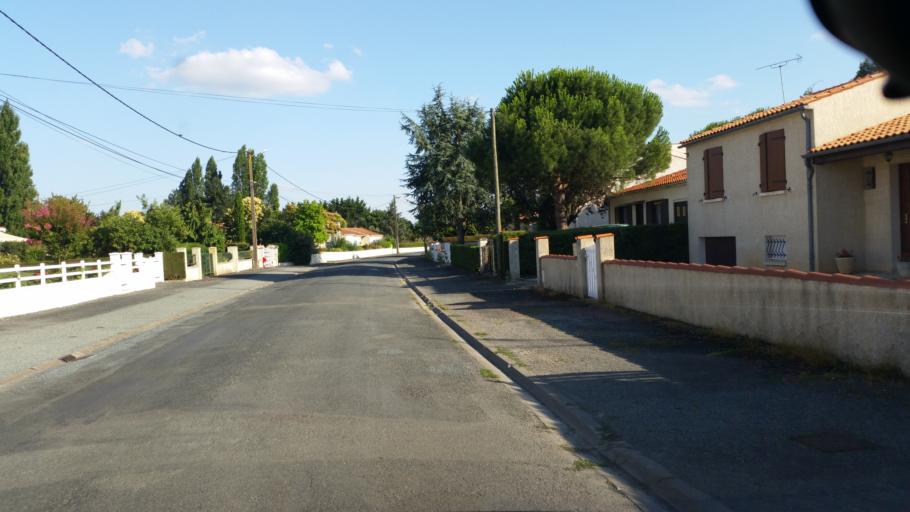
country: FR
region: Poitou-Charentes
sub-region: Departement de la Charente-Maritime
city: Marans
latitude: 46.3061
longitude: -0.9838
